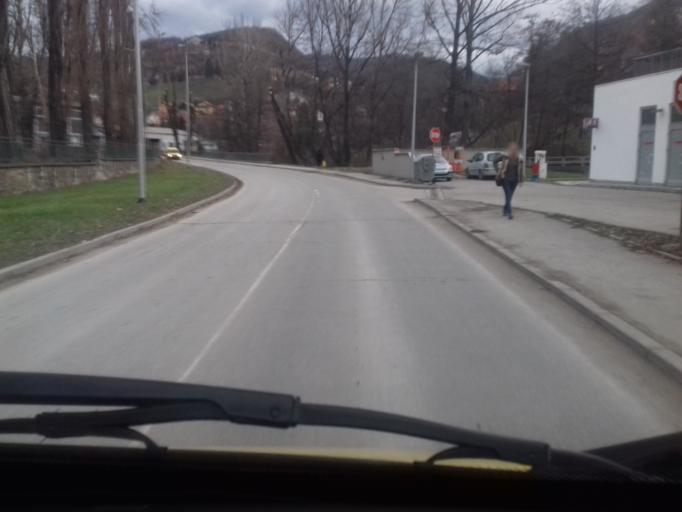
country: BA
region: Federation of Bosnia and Herzegovina
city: Zenica
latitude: 44.2083
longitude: 17.9272
